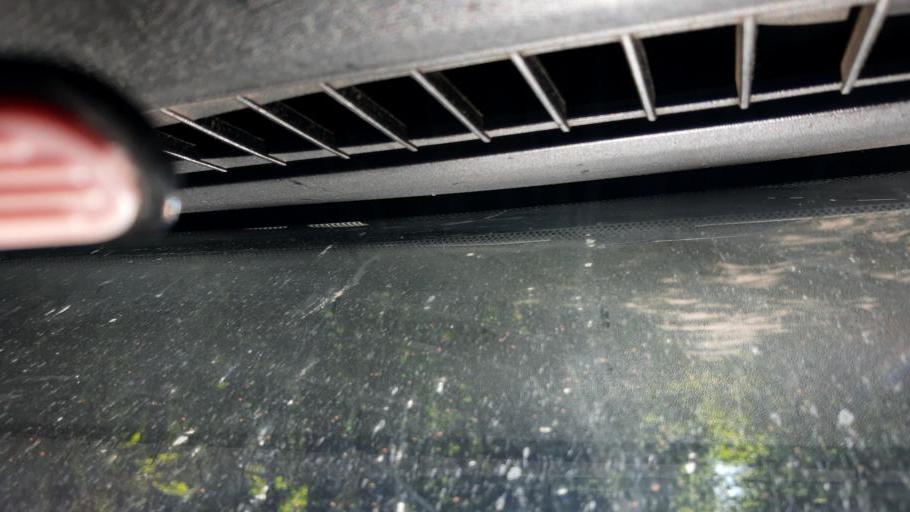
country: RU
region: Bashkortostan
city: Ufa
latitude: 54.6704
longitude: 56.0633
